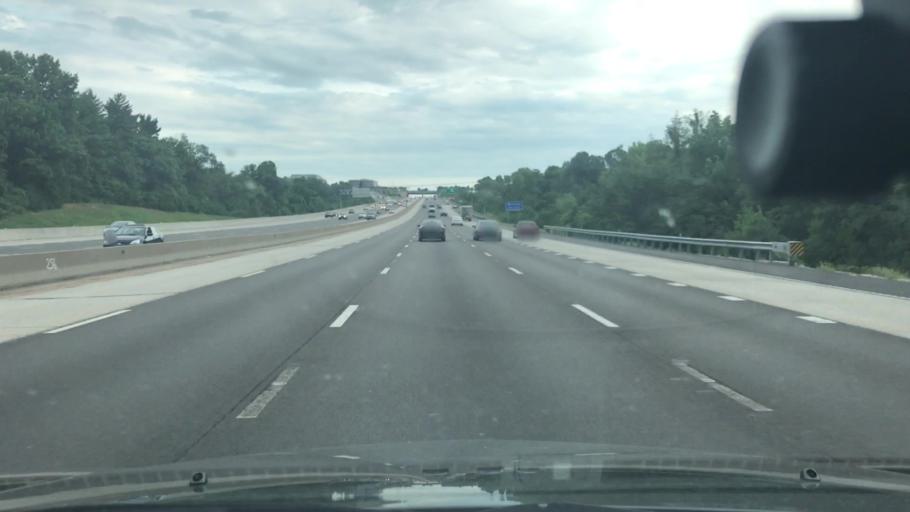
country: US
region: Missouri
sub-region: Saint Louis County
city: Creve Coeur
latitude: 38.6828
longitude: -90.4499
